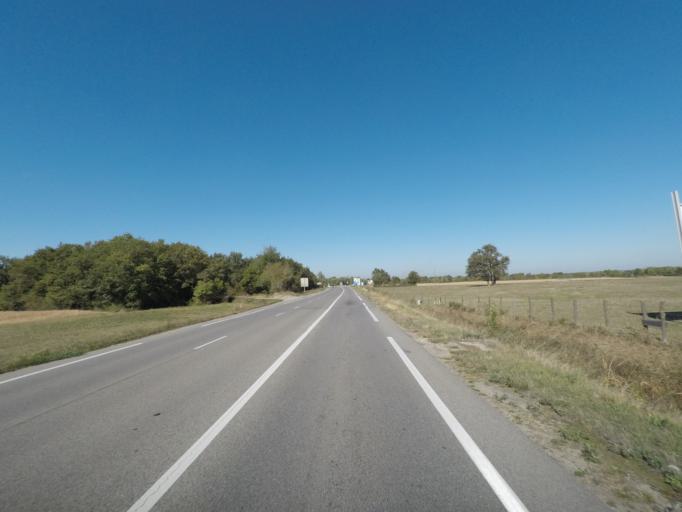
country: FR
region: Rhone-Alpes
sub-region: Departement de l'Ain
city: Attignat
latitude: 46.2571
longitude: 5.1789
